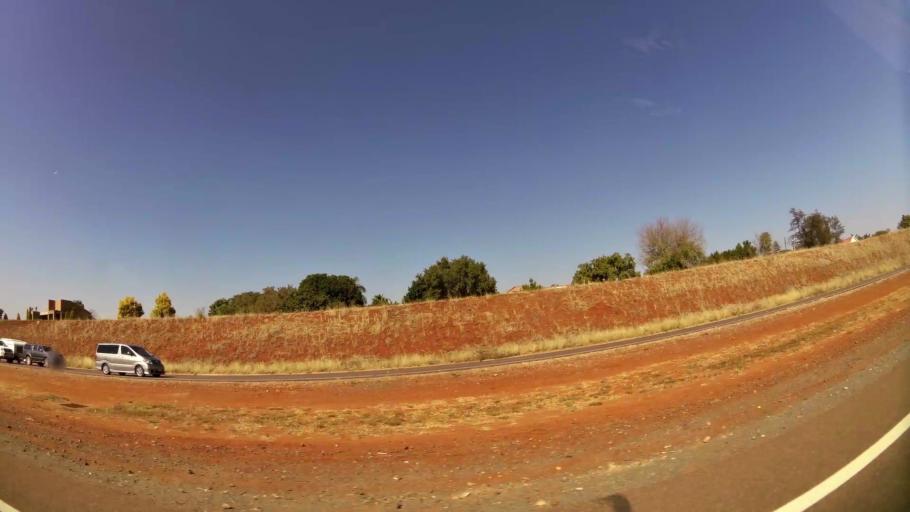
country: ZA
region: North-West
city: Ga-Rankuwa
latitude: -25.6558
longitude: 28.0980
